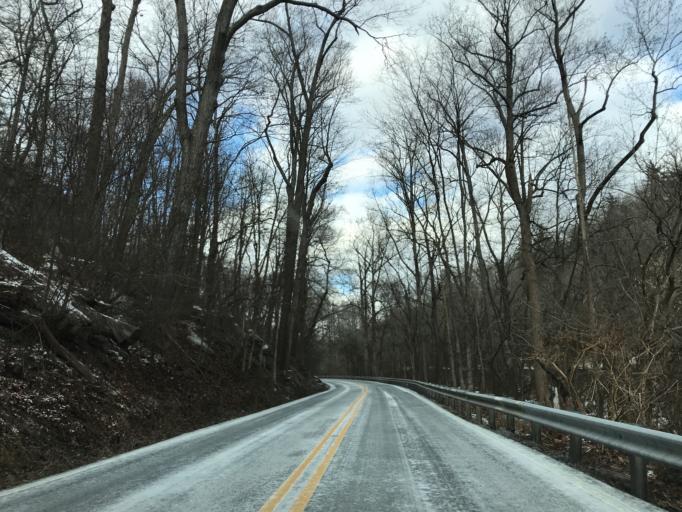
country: US
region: Maryland
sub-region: Harford County
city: Jarrettsville
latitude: 39.6351
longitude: -76.4115
